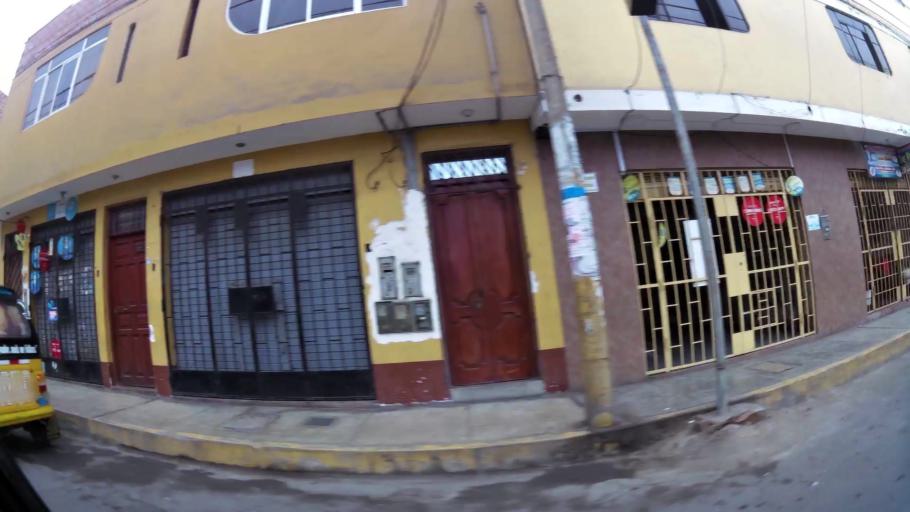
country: PE
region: Lima
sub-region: Barranca
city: Barranca
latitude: -10.7496
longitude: -77.7644
